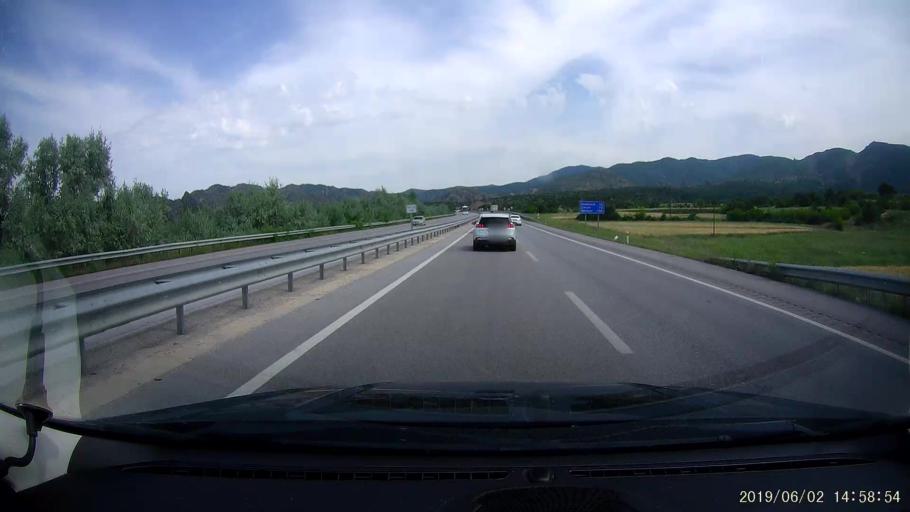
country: TR
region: Corum
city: Osmancik
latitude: 40.9752
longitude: 34.6865
